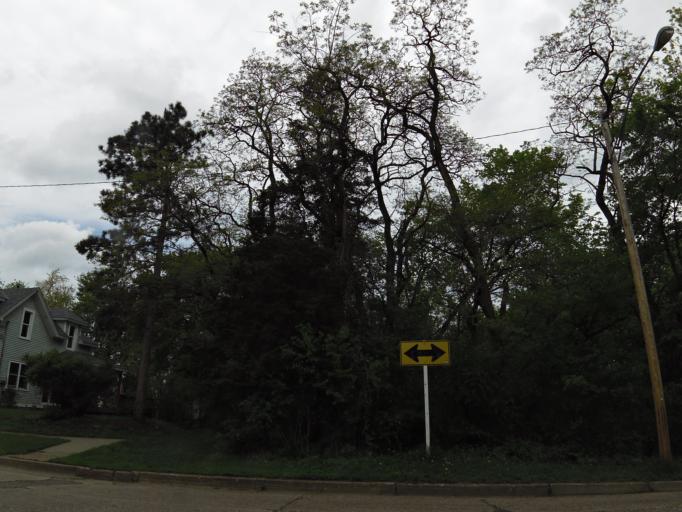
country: US
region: Wisconsin
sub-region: Saint Croix County
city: North Hudson
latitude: 44.9849
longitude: -92.7541
